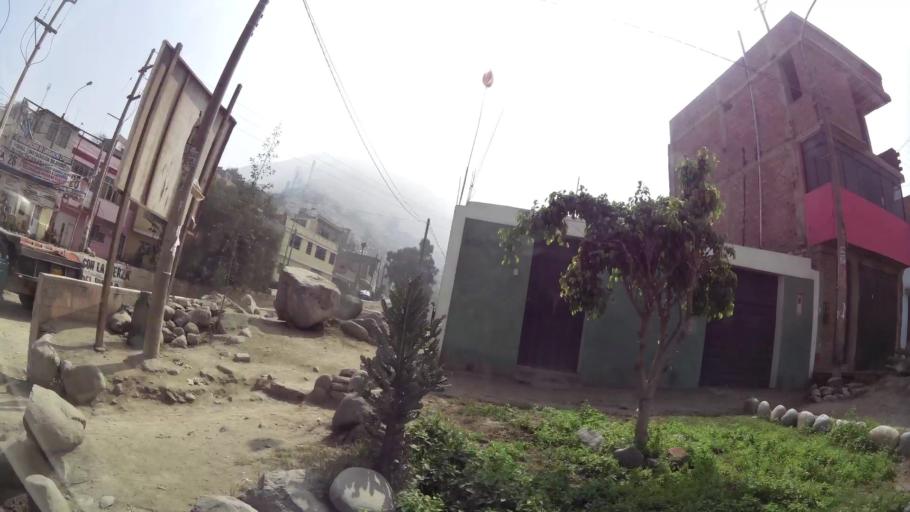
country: PE
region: Lima
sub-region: Lima
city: Asentamiento Humano Nicolas de Pierola
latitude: -11.9412
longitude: -76.7028
